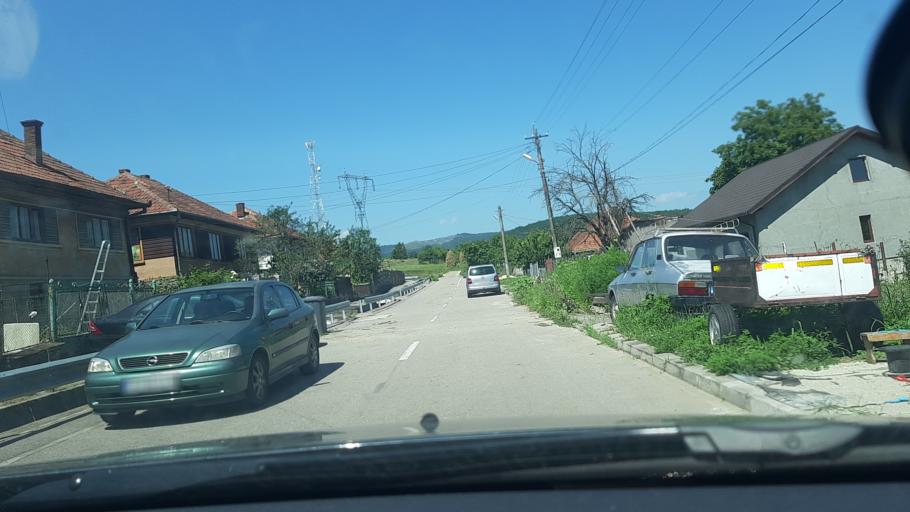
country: RO
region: Hunedoara
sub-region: Comuna Teliucu Inferior
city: Teliucu Inferior
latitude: 45.7038
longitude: 22.8894
